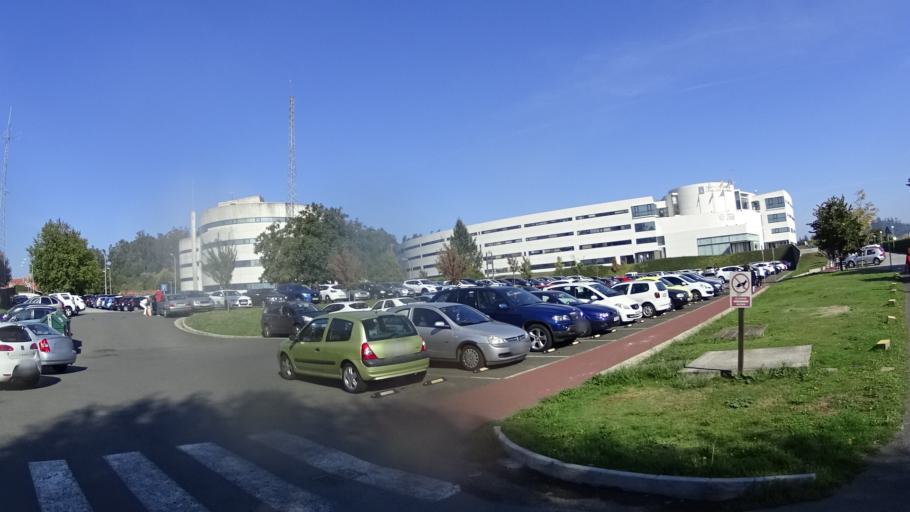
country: ES
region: Galicia
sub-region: Provincia da Coruna
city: Santiago de Compostela
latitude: 42.8870
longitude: -8.5175
